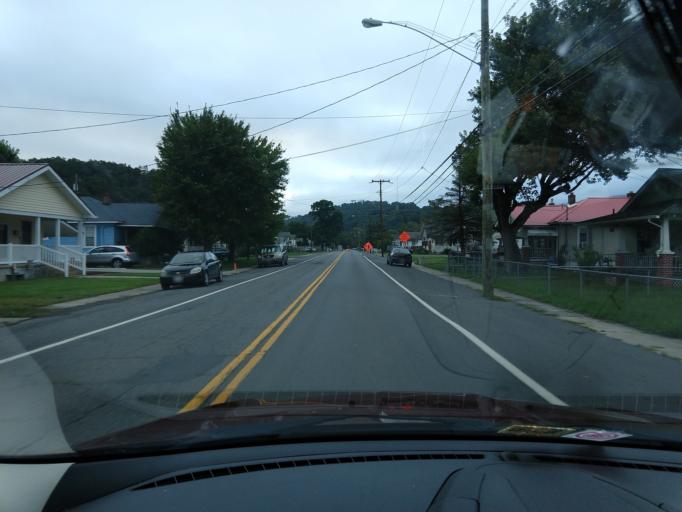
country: US
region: Virginia
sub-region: City of Covington
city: Fairlawn
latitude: 37.7649
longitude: -79.9972
